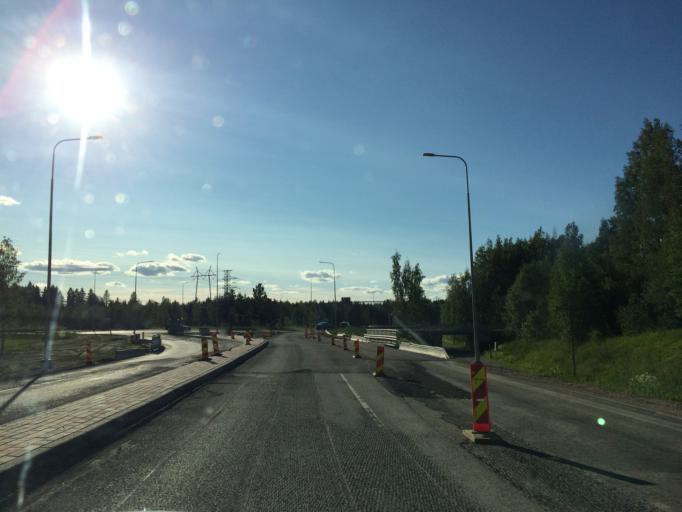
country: FI
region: Haeme
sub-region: Haemeenlinna
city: Haemeenlinna
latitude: 60.9834
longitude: 24.5094
